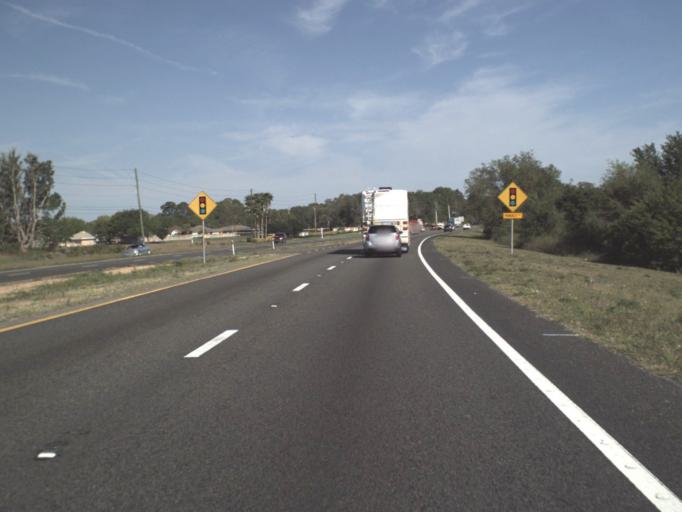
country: US
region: Florida
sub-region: Lake County
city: Yalaha
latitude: 28.6597
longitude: -81.8491
